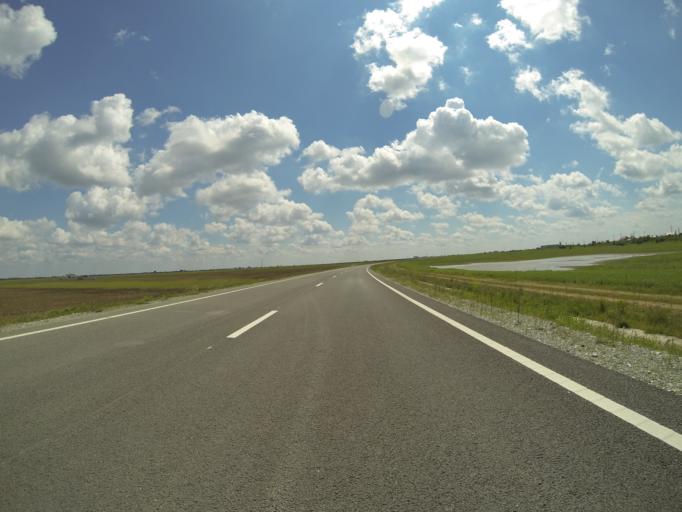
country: RO
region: Dolj
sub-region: Comuna Carcea
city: Carcea
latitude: 44.2692
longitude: 23.9120
